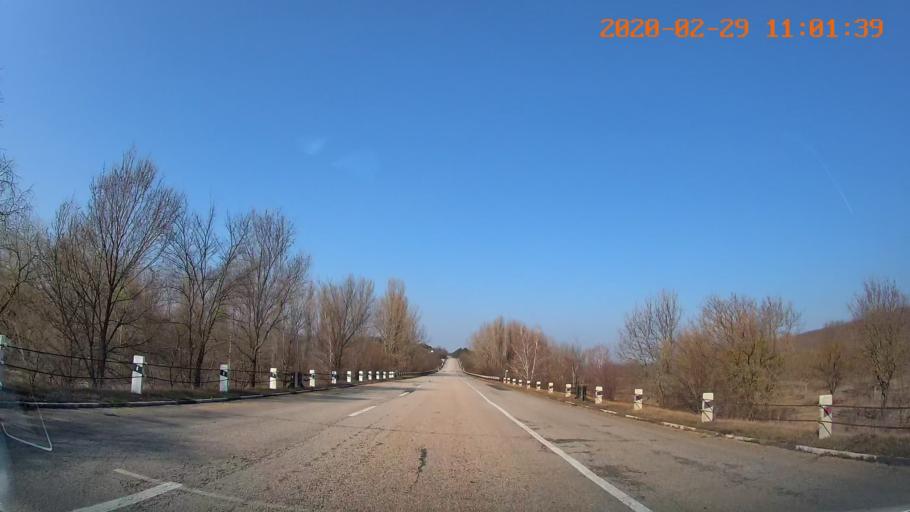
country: MD
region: Telenesti
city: Grigoriopol
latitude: 47.1658
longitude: 29.2541
